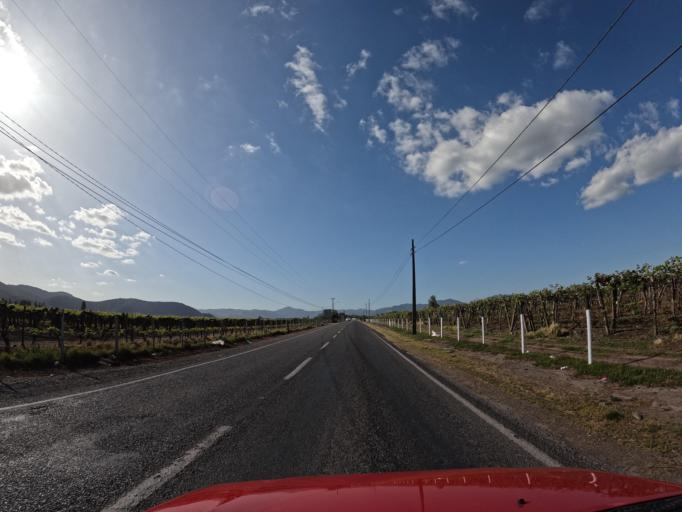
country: CL
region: Maule
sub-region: Provincia de Curico
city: Rauco
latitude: -34.9185
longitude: -71.2771
